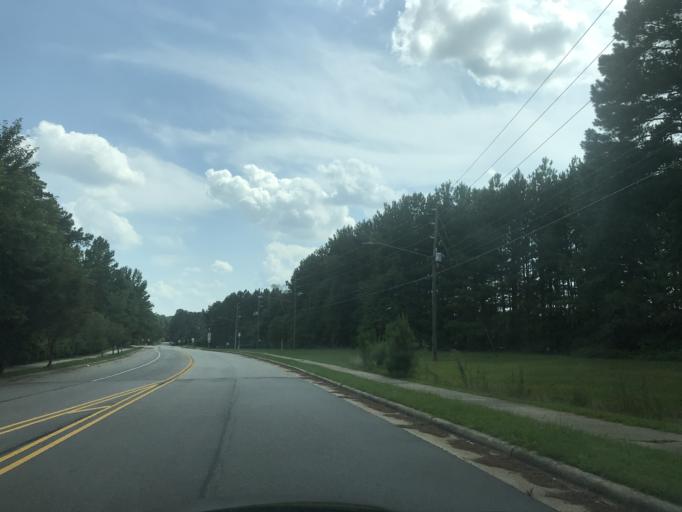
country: US
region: North Carolina
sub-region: Wake County
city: West Raleigh
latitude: 35.8924
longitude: -78.6549
